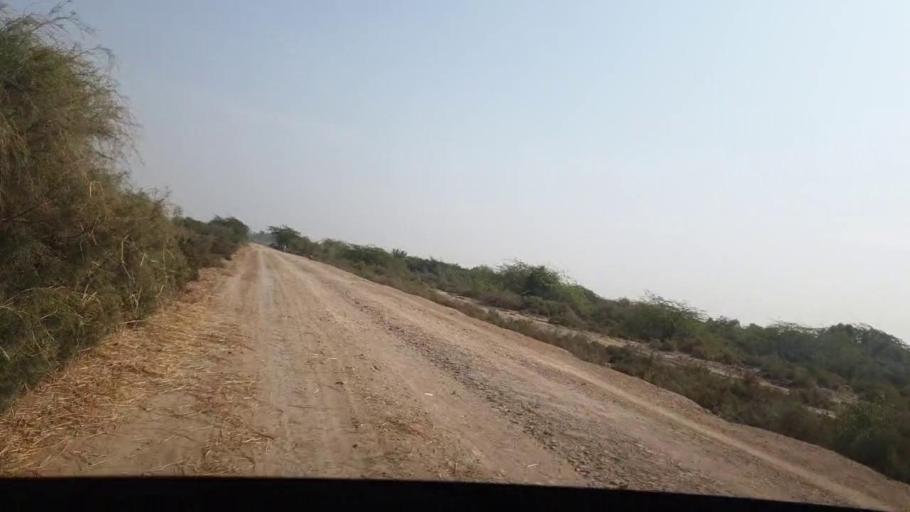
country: PK
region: Sindh
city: Chuhar Jamali
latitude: 24.2694
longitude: 67.9337
